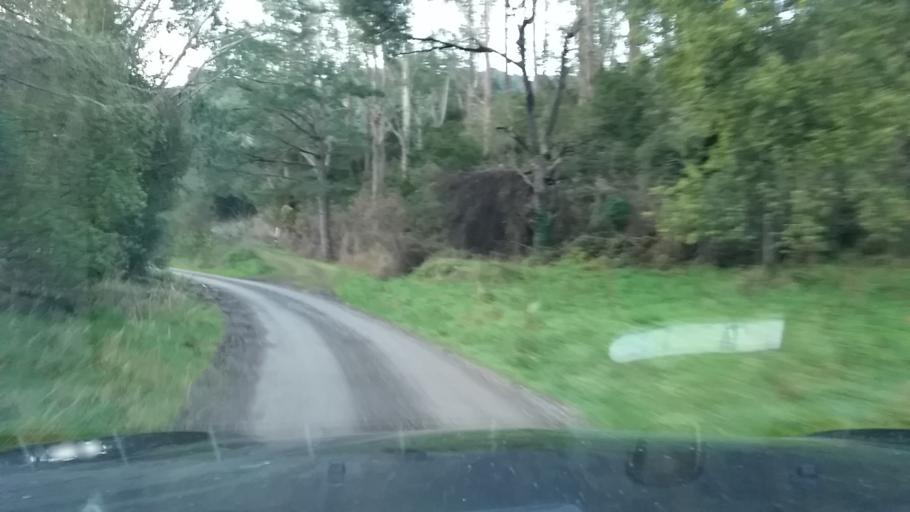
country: NZ
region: Marlborough
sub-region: Marlborough District
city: Blenheim
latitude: -41.4717
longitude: 173.7454
